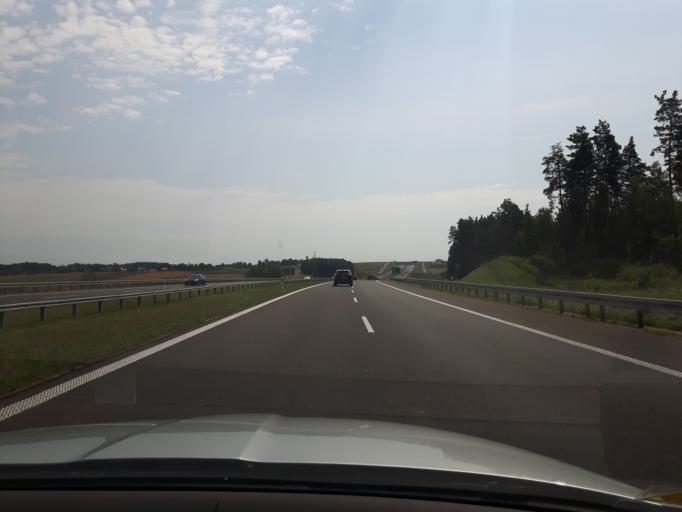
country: PL
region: Warmian-Masurian Voivodeship
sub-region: Powiat nidzicki
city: Nidzica
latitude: 53.3671
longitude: 20.3885
